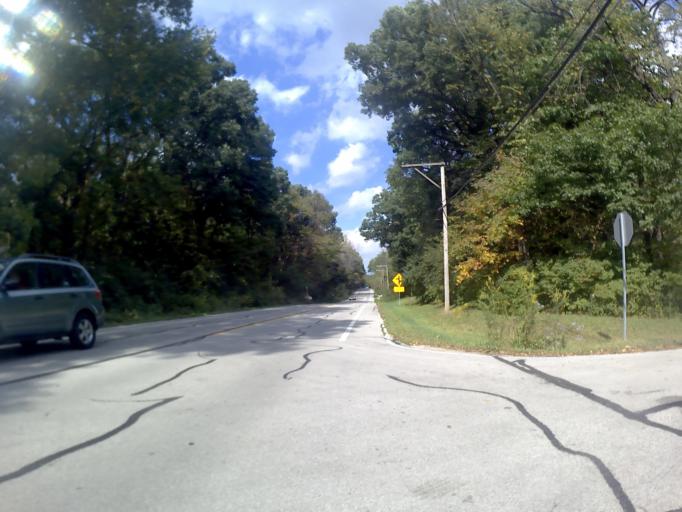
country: US
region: Illinois
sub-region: Will County
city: Bolingbrook
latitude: 41.7208
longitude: -88.1025
